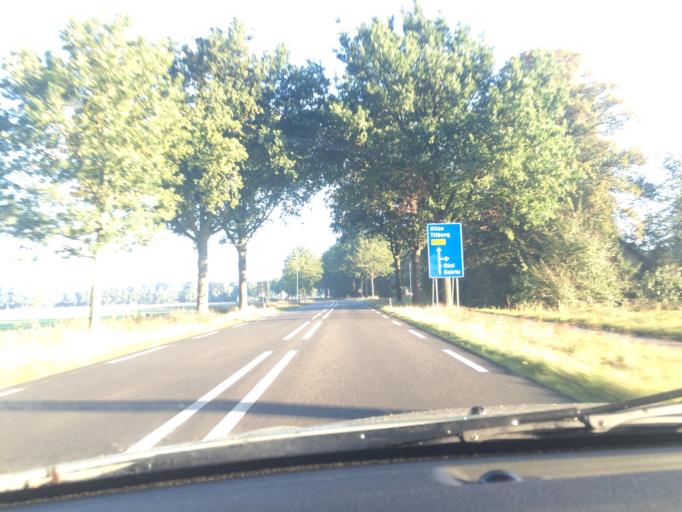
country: NL
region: North Brabant
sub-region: Gemeente Baarle-Nassau
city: Baarle-Nassau
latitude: 51.4998
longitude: 4.9660
